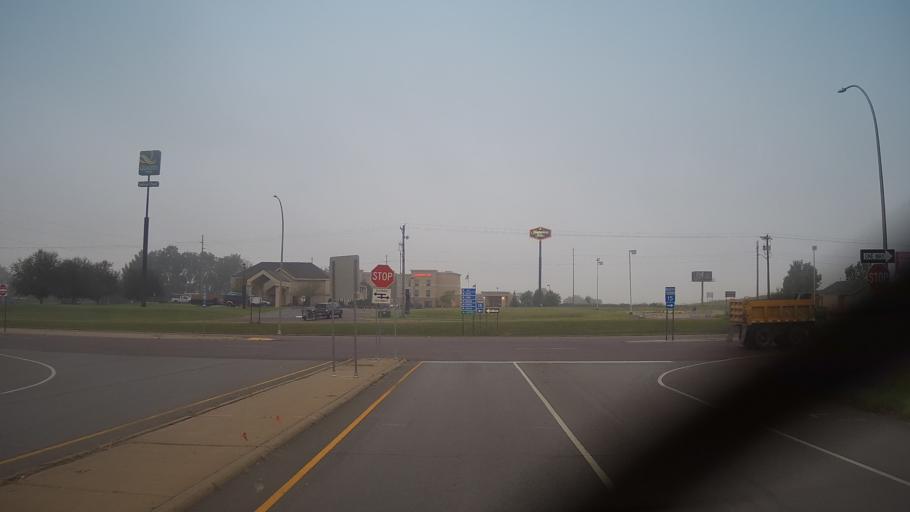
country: US
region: Minnesota
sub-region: Martin County
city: Fairmont
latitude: 43.6776
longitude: -94.4472
